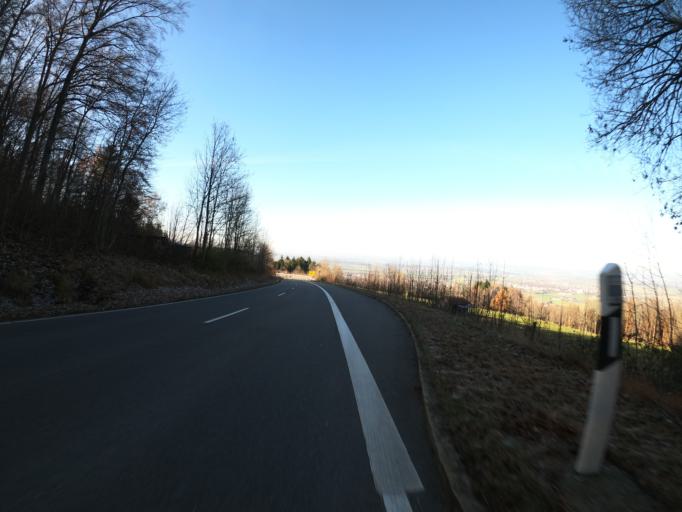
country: DE
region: Baden-Wuerttemberg
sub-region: Regierungsbezirk Stuttgart
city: Gammelshausen
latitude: 48.6330
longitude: 9.6594
